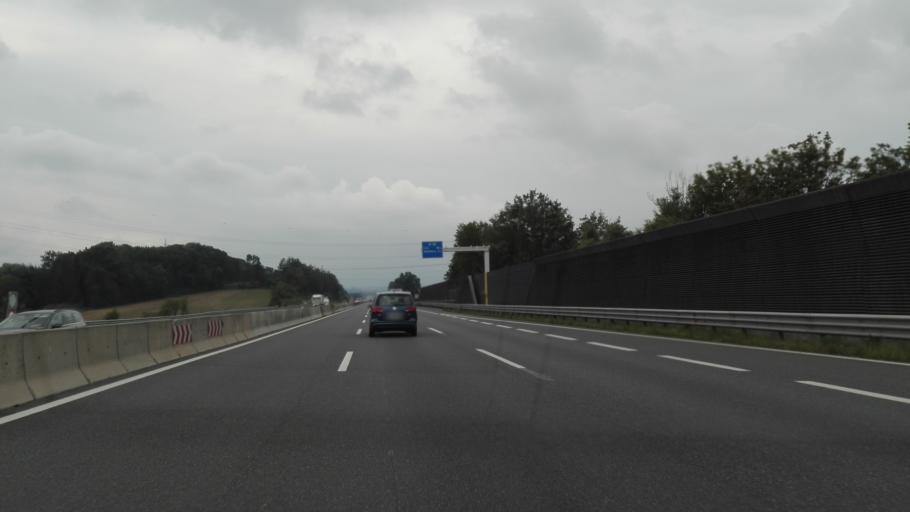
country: AT
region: Lower Austria
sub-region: Politischer Bezirk Melk
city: Ybbs an der Donau
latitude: 48.1527
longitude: 15.0965
